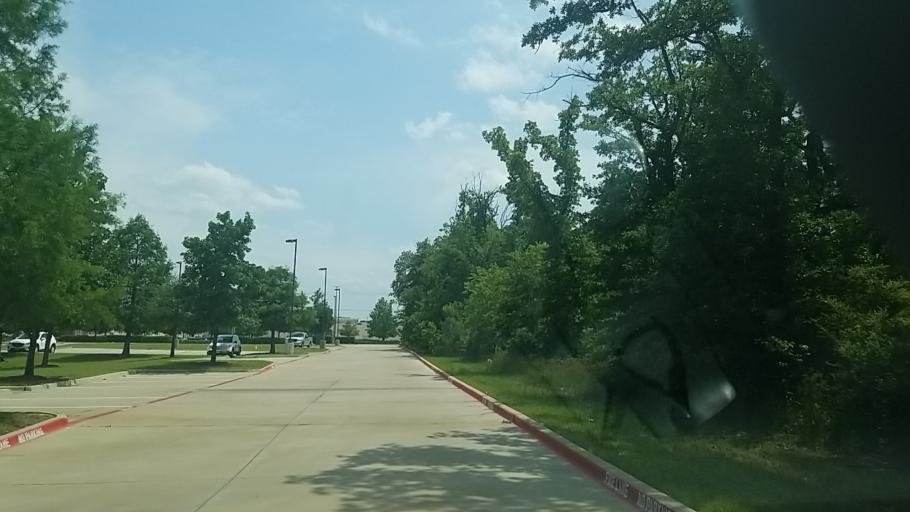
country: US
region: Texas
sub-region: Denton County
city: Denton
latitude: 33.1971
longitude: -97.0946
